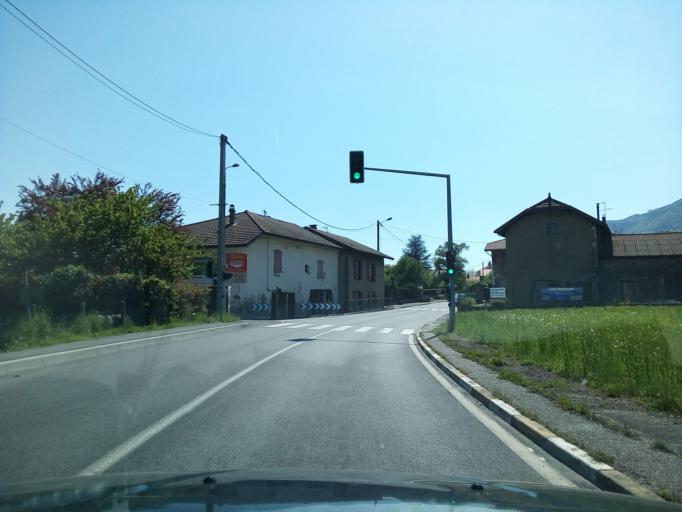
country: FR
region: Rhone-Alpes
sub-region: Departement de l'Isere
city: Saint-Vincent-de-Mercuze
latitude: 45.3834
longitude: 5.9711
